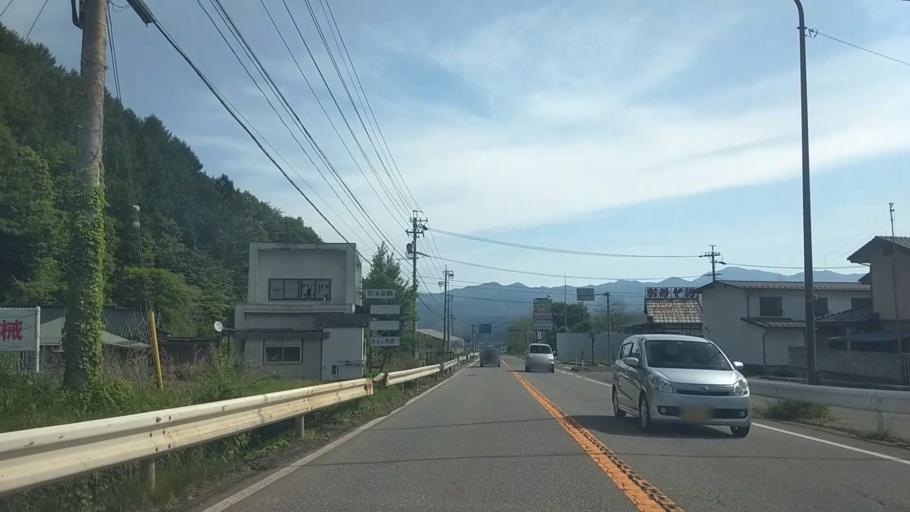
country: JP
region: Nagano
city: Saku
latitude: 36.0622
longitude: 138.4699
